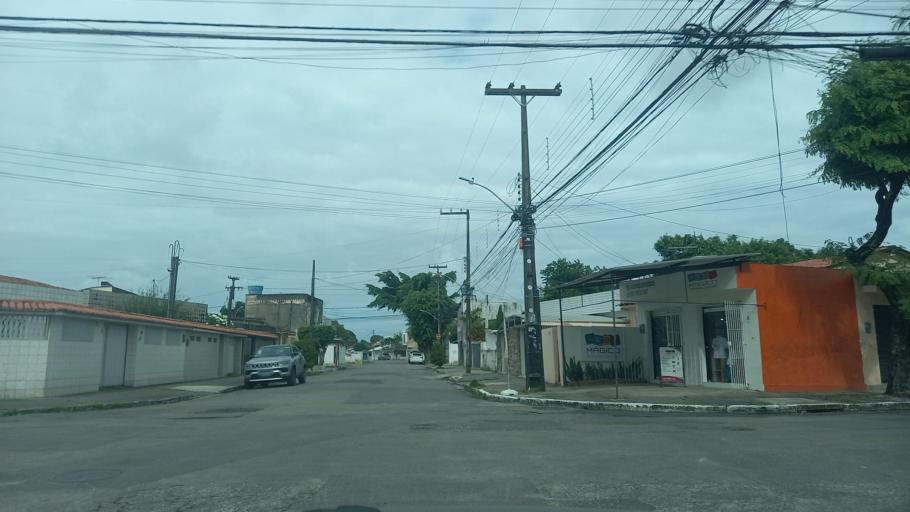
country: BR
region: Pernambuco
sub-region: Recife
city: Recife
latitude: -8.1117
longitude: -34.9227
